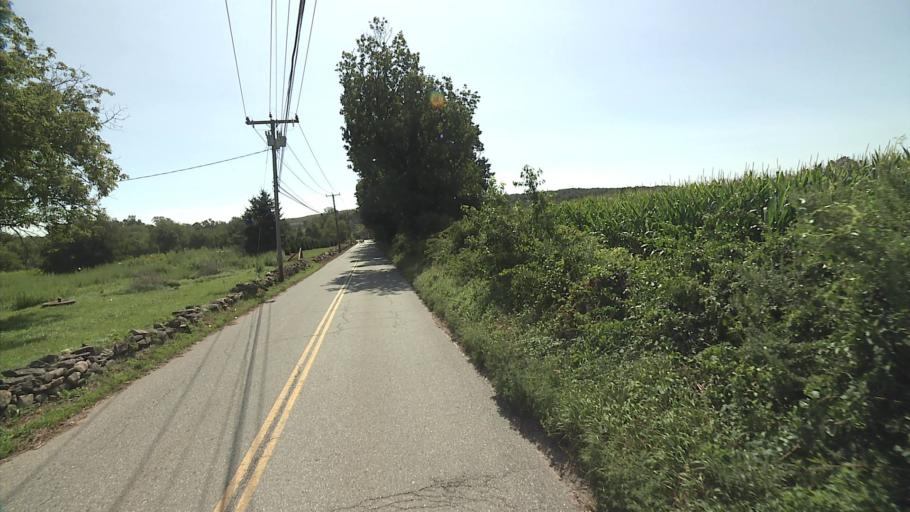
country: US
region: Connecticut
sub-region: Windham County
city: South Windham
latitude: 41.6376
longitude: -72.1715
